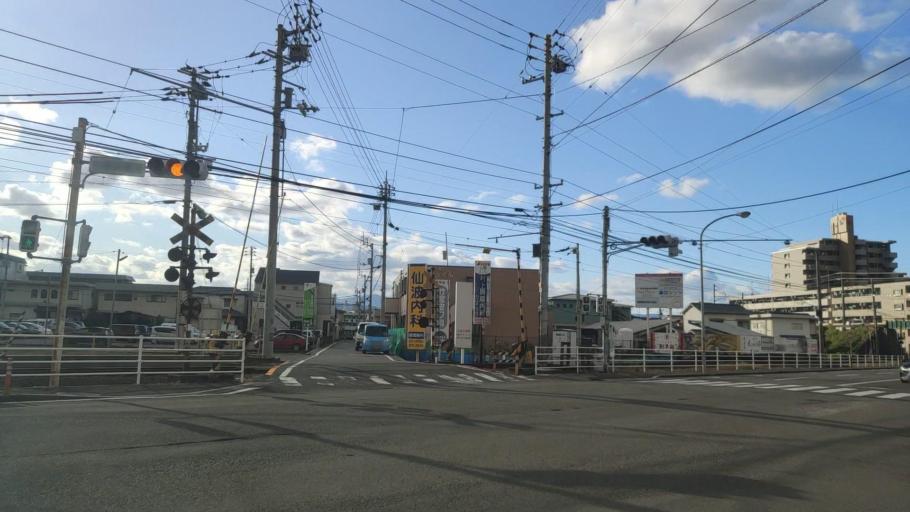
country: JP
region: Ehime
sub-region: Shikoku-chuo Shi
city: Matsuyama
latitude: 33.8303
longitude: 132.7525
